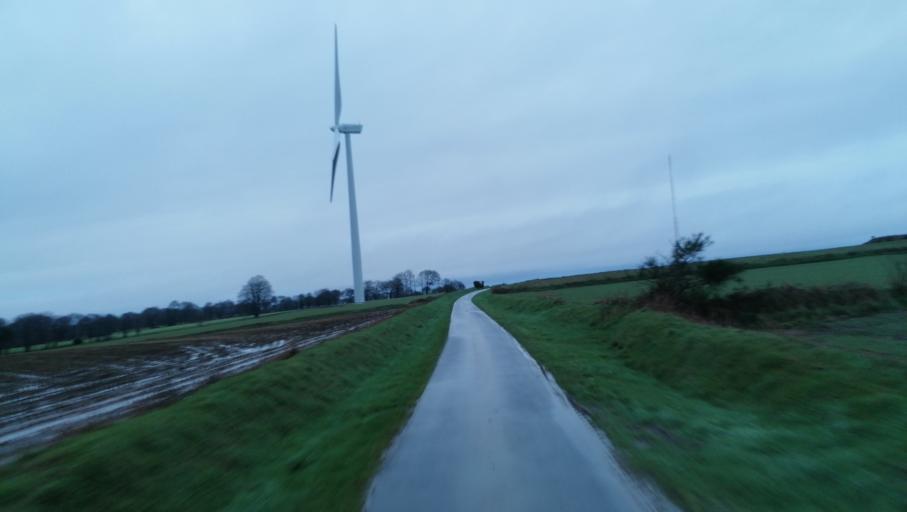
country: FR
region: Brittany
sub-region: Departement des Cotes-d'Armor
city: Lanrodec
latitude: 48.4846
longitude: -2.9959
